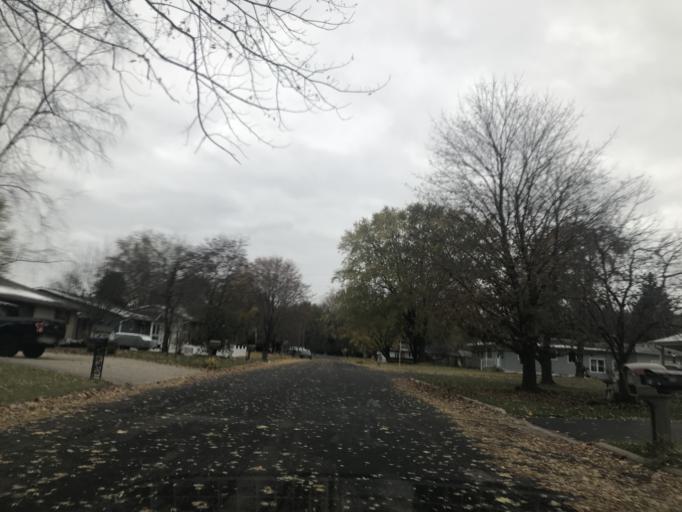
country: US
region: Wisconsin
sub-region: Marinette County
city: Marinette
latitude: 45.0939
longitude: -87.6518
